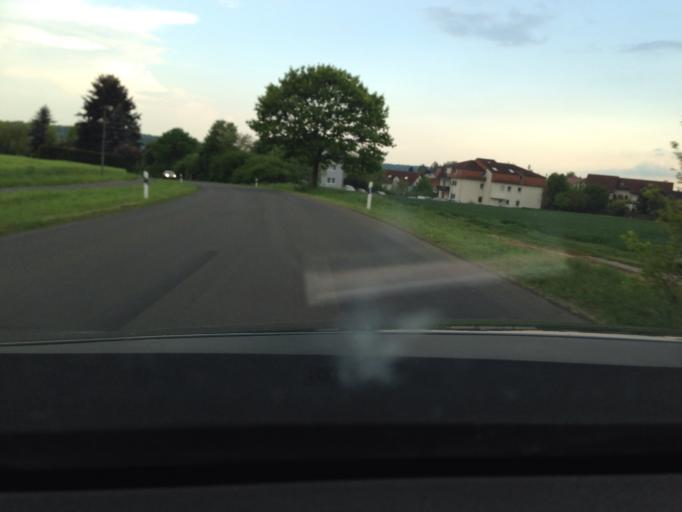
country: DE
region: Hesse
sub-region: Regierungsbezirk Giessen
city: Grossen Buseck
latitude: 50.5825
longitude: 8.7585
